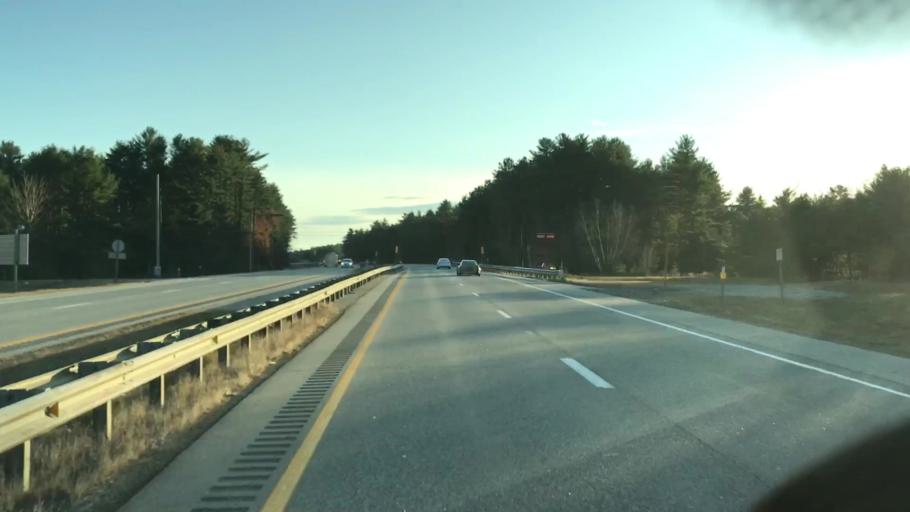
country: US
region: Maine
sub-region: Cumberland County
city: New Gloucester
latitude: 43.9986
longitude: -70.3082
